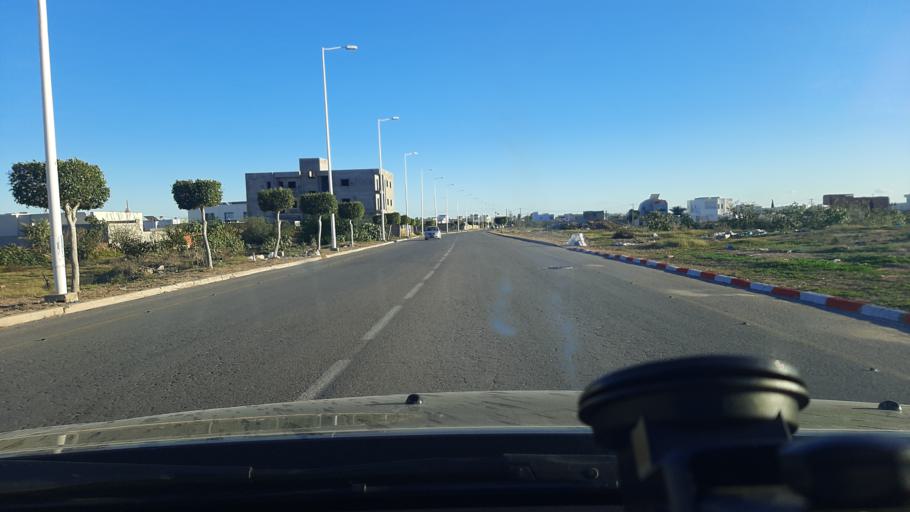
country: TN
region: Safaqis
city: Sfax
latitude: 34.8049
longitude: 10.7146
